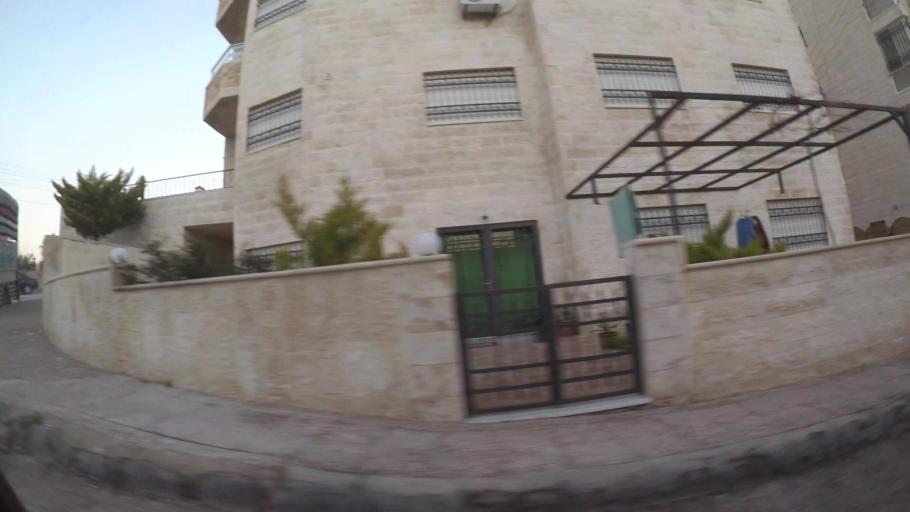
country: JO
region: Amman
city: Al Bunayyat ash Shamaliyah
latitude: 31.8942
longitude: 35.9231
